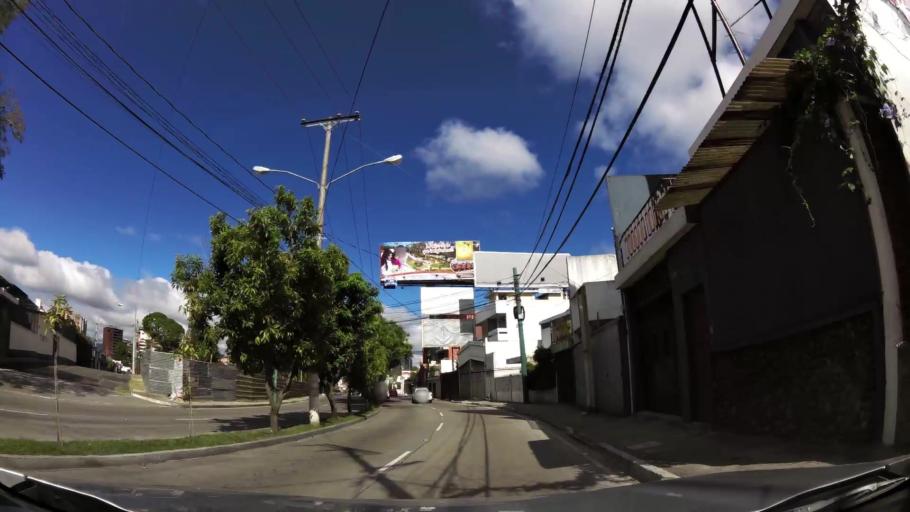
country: GT
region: Guatemala
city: Santa Catarina Pinula
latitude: 14.5935
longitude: -90.5047
